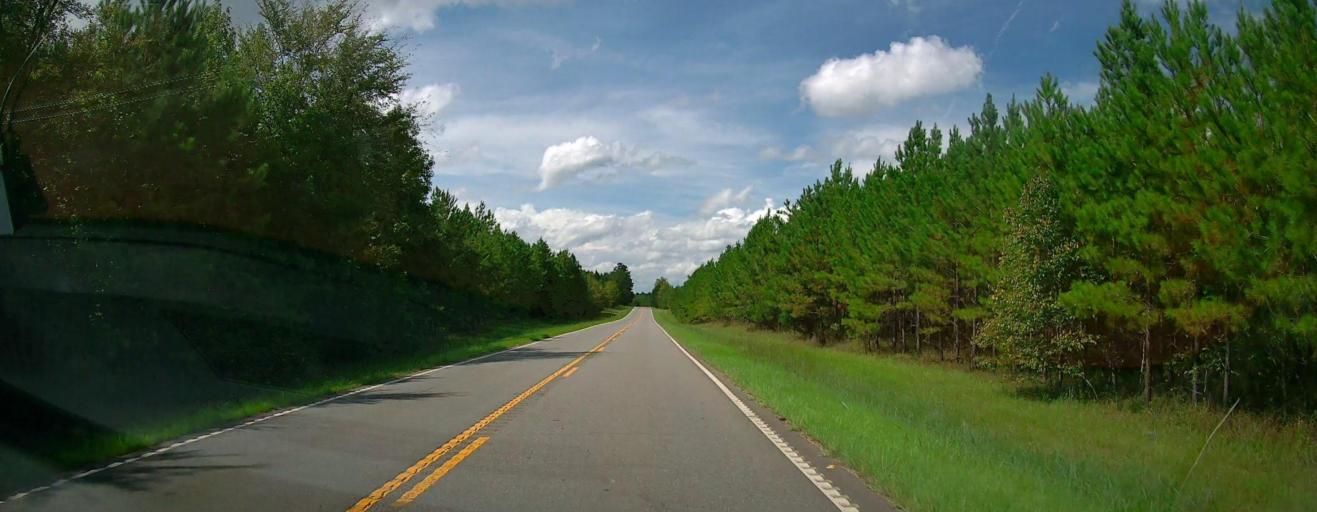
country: US
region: Georgia
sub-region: Talbot County
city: Talbotton
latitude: 32.6597
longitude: -84.5113
